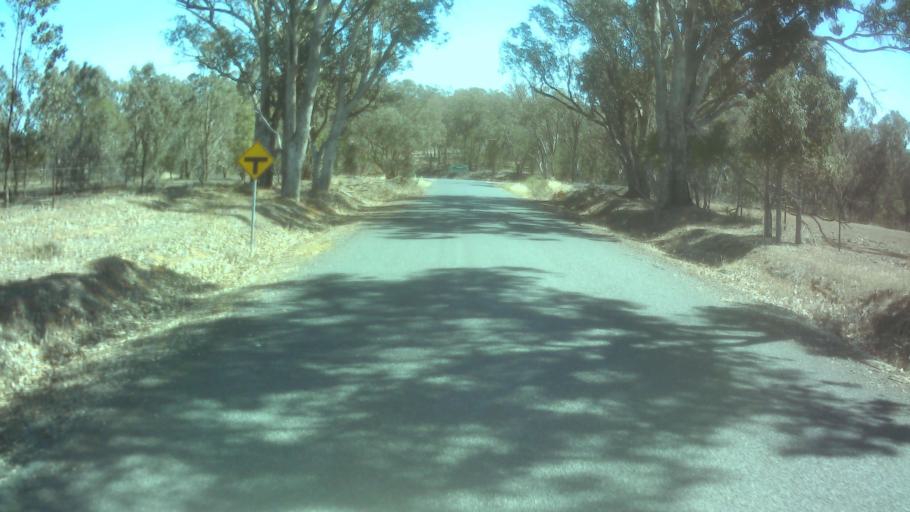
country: AU
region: New South Wales
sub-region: Weddin
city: Grenfell
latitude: -33.9400
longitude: 148.3849
